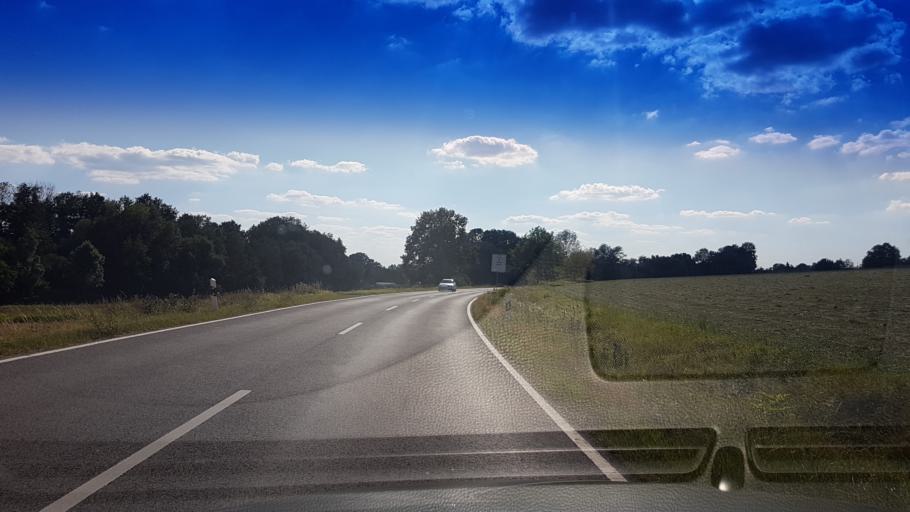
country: DE
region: Bavaria
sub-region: Upper Franconia
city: Litzendorf
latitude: 49.8709
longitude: 11.0348
